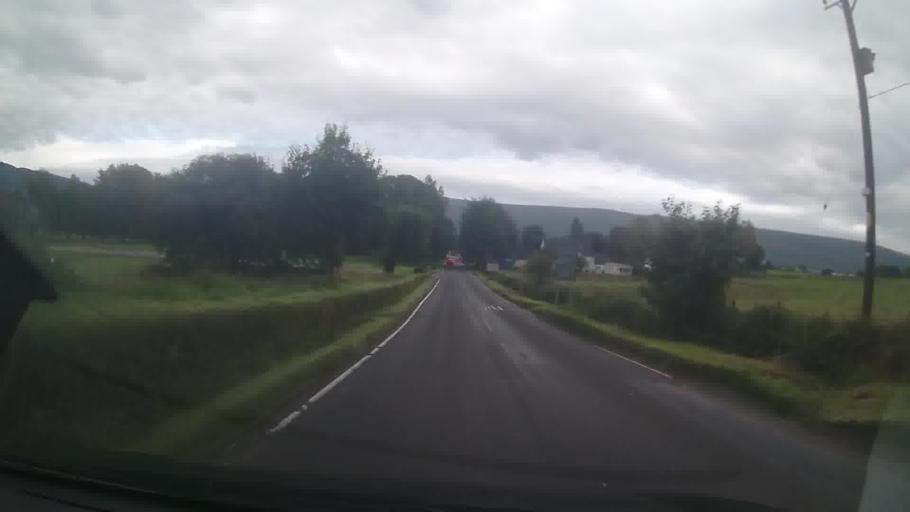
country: GB
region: Scotland
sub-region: Argyll and Bute
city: Garelochhead
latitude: 56.2332
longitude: -5.0799
